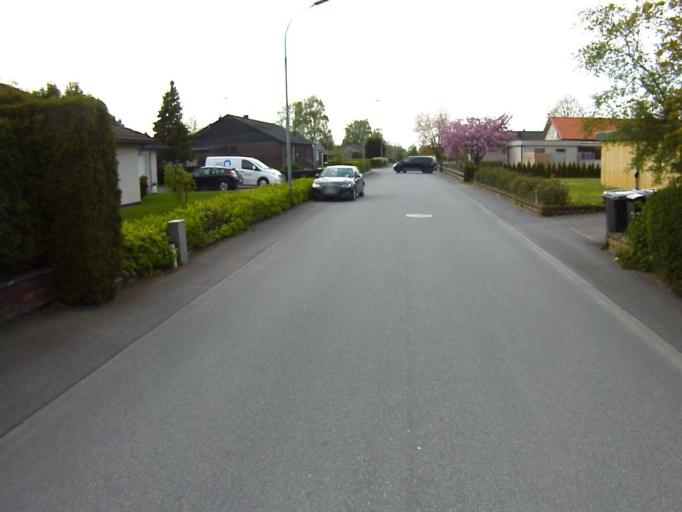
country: SE
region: Skane
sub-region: Kristianstads Kommun
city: Fjalkinge
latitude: 56.0470
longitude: 14.2798
